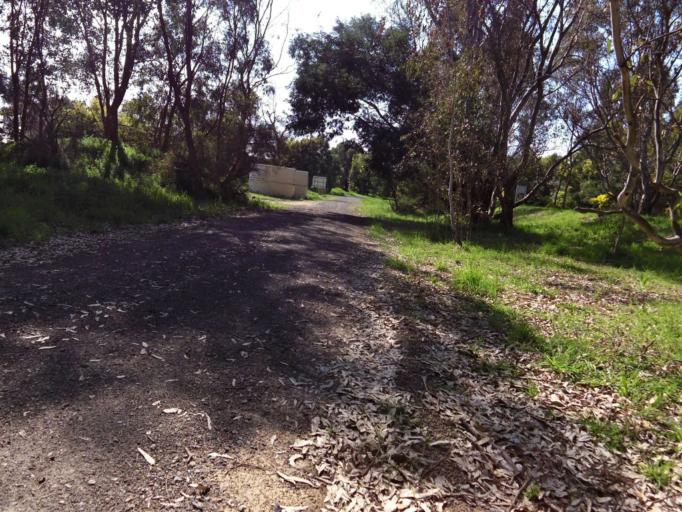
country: AU
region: Victoria
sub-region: Murrindindi
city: Alexandra
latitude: -37.1504
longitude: 145.5829
